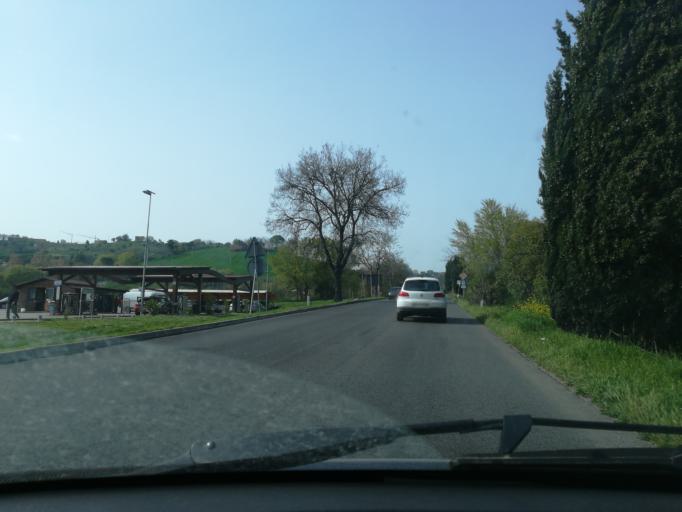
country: IT
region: The Marches
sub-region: Provincia di Macerata
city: Piediripa
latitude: 43.2822
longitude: 13.4849
